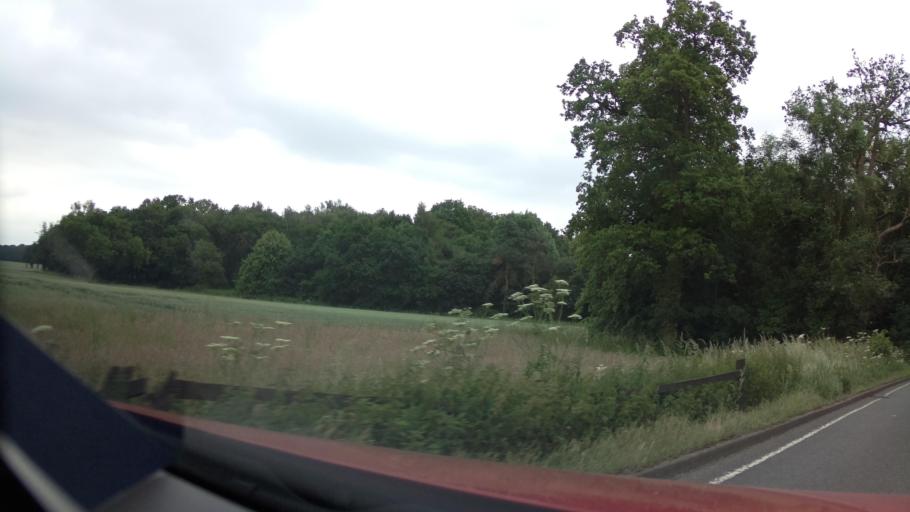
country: GB
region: England
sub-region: Derbyshire
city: Rodsley
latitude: 52.8999
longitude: -1.7668
